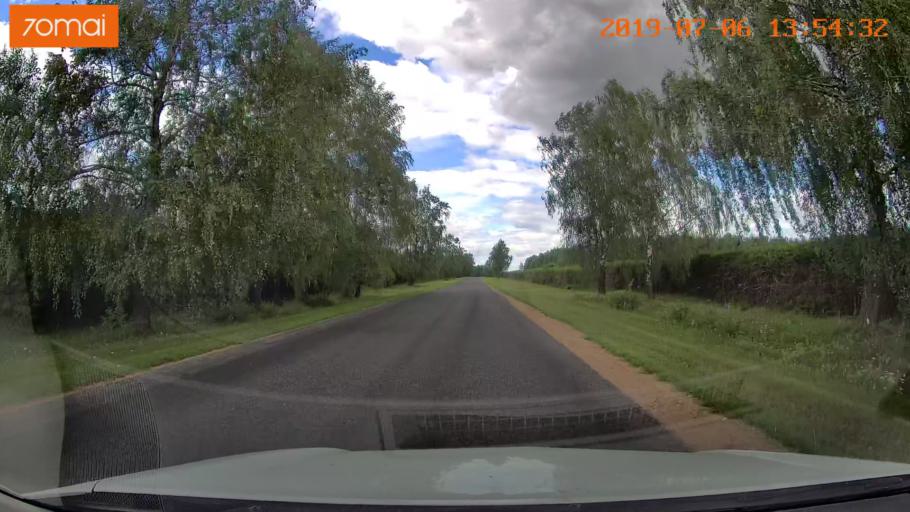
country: BY
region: Minsk
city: Ivyanyets
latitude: 53.7467
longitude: 26.8195
